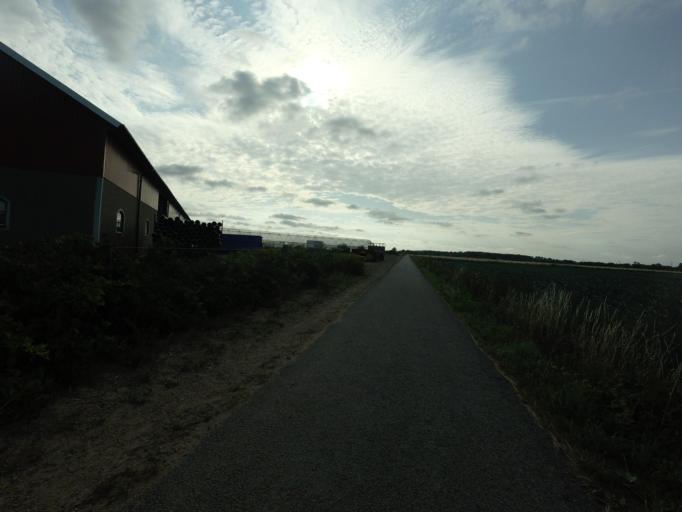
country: SE
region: Skane
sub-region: Hoganas Kommun
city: Hoganas
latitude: 56.1852
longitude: 12.6398
